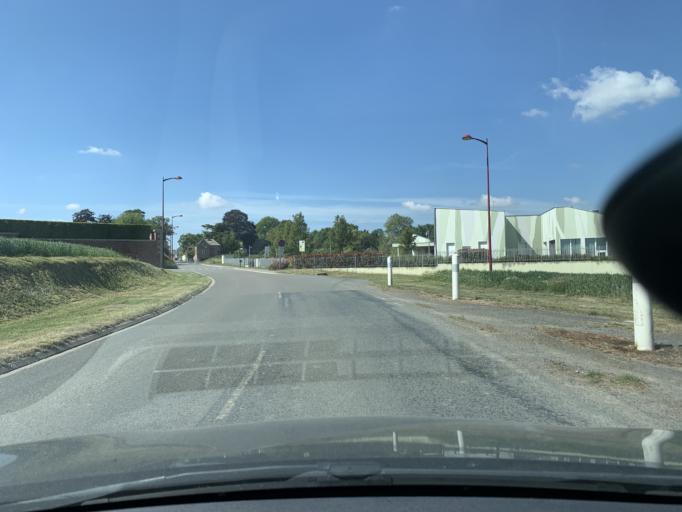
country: FR
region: Nord-Pas-de-Calais
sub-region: Departement du Pas-de-Calais
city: Oisy-le-Verger
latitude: 50.2551
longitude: 3.1268
